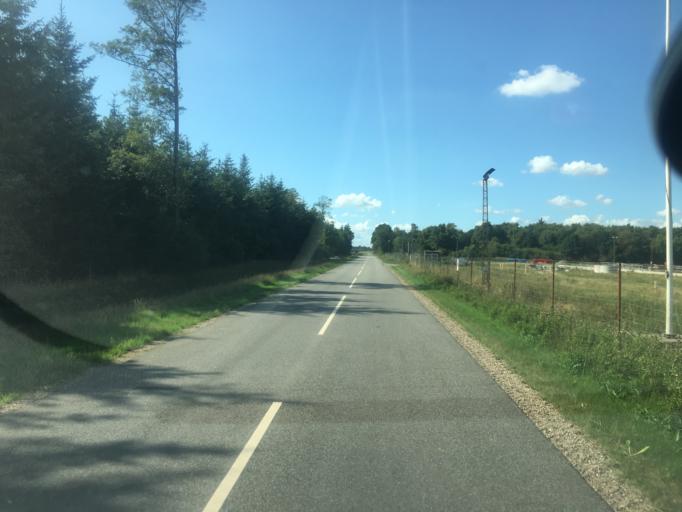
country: DE
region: Schleswig-Holstein
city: Ellhoft
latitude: 54.9653
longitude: 8.9768
